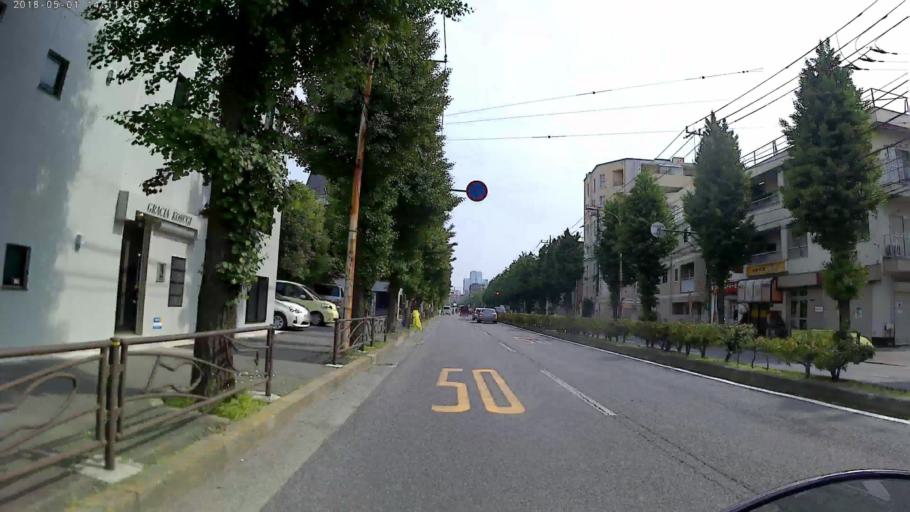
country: JP
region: Kanagawa
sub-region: Kawasaki-shi
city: Kawasaki
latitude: 35.5731
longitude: 139.6691
